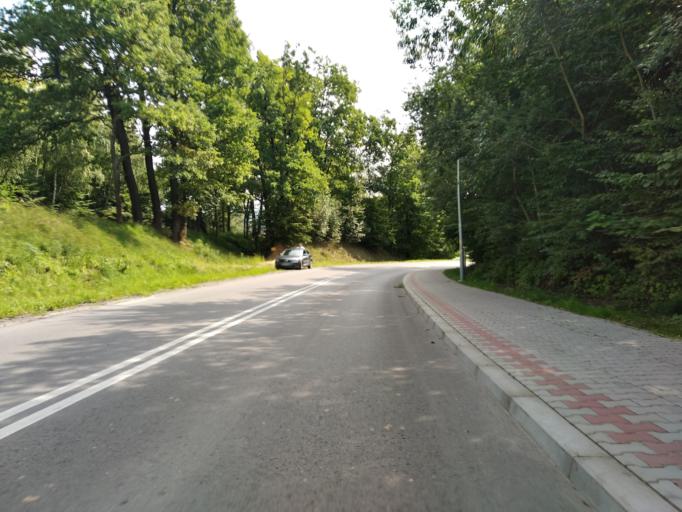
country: PL
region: Subcarpathian Voivodeship
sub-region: Powiat ropczycko-sedziszowski
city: Ropczyce
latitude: 50.0609
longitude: 21.6137
